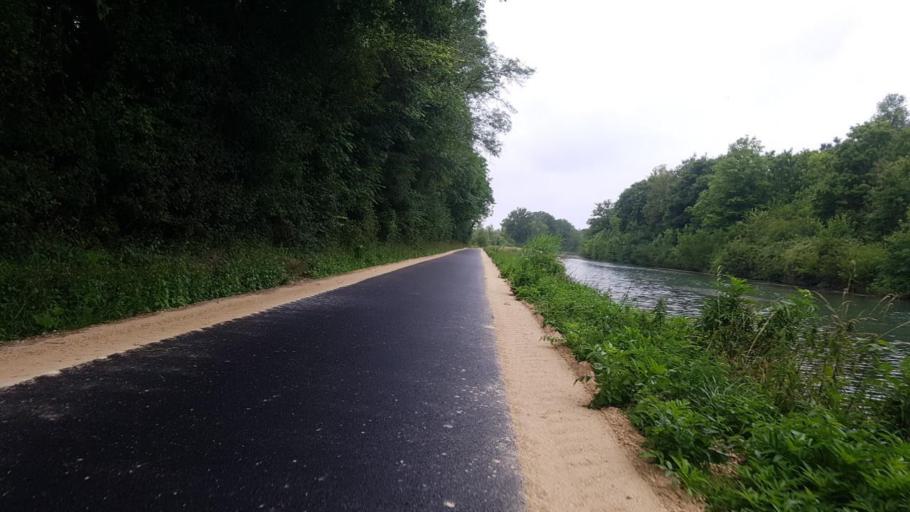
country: FR
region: Champagne-Ardenne
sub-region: Departement de la Marne
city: Vitry-le-Francois
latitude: 48.7954
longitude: 4.5293
